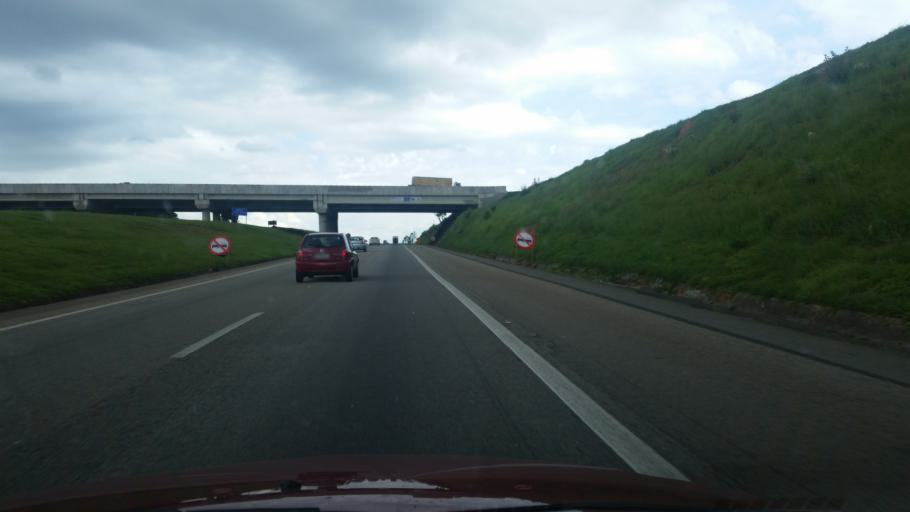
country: BR
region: Sao Paulo
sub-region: Itu
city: Itu
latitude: -23.3947
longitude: -47.3539
